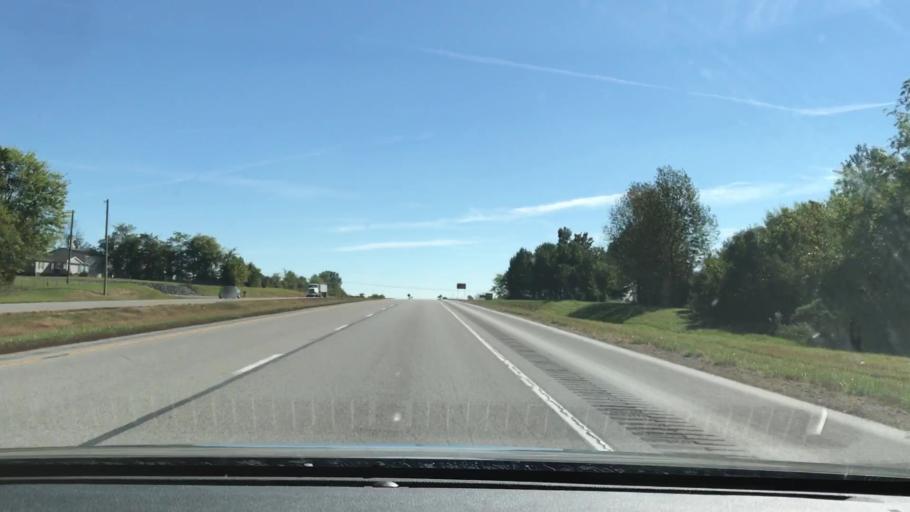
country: US
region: Kentucky
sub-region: Todd County
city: Elkton
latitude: 36.8238
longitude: -87.2053
